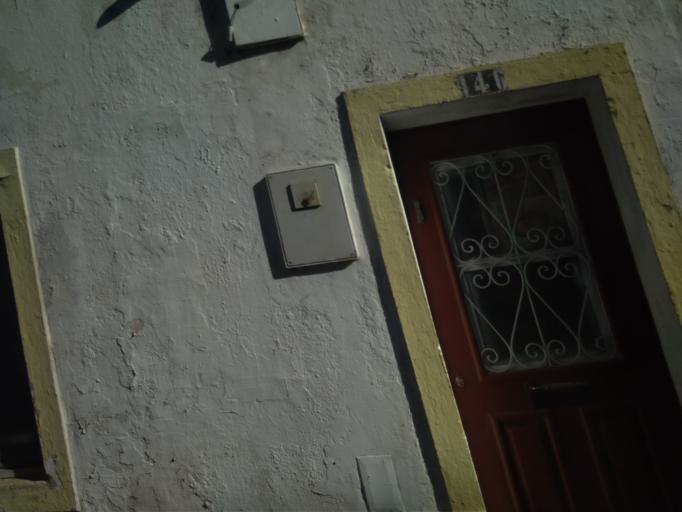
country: PT
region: Faro
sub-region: Faro
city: Faro
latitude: 37.0206
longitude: -7.9388
